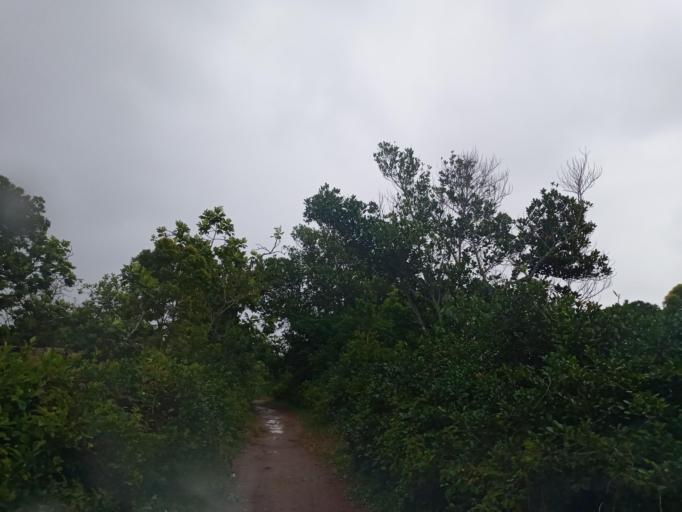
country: MG
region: Atsimo-Atsinanana
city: Vohipaho
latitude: -23.8346
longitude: 47.5479
